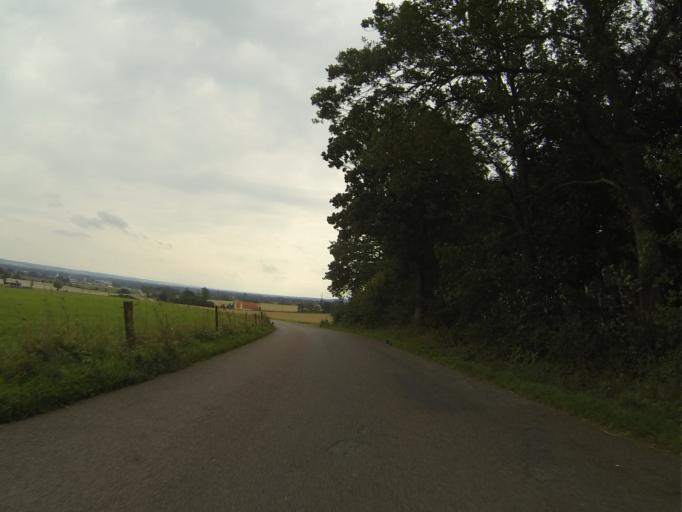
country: SE
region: Skane
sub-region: Eslovs Kommun
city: Eslov
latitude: 55.7245
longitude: 13.3146
